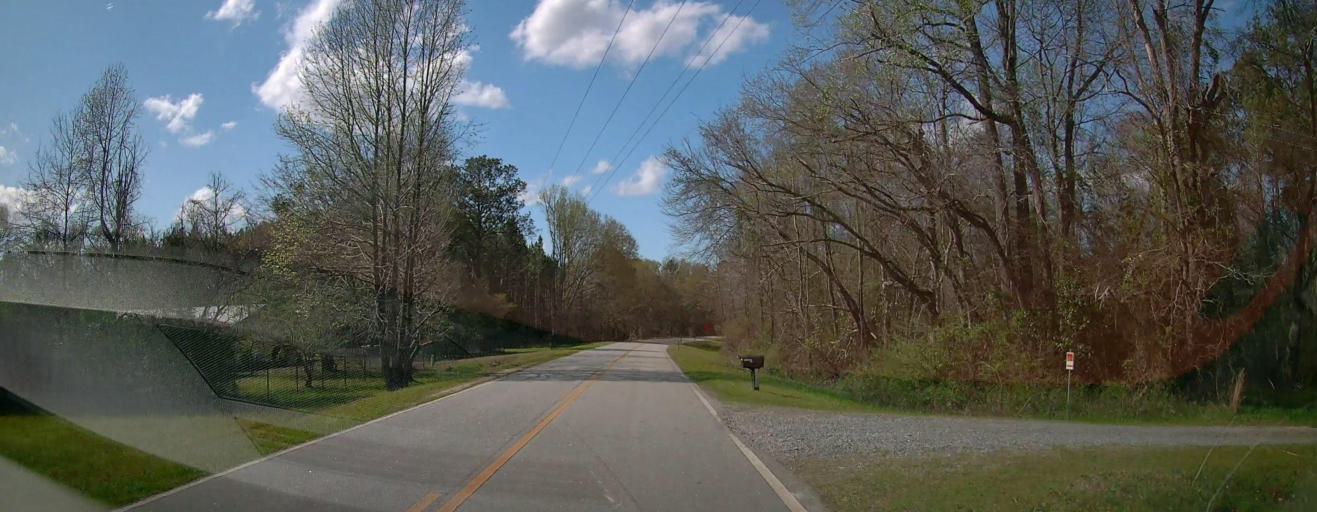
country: US
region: Georgia
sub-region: Wilkinson County
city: Gordon
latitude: 32.8455
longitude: -83.4461
